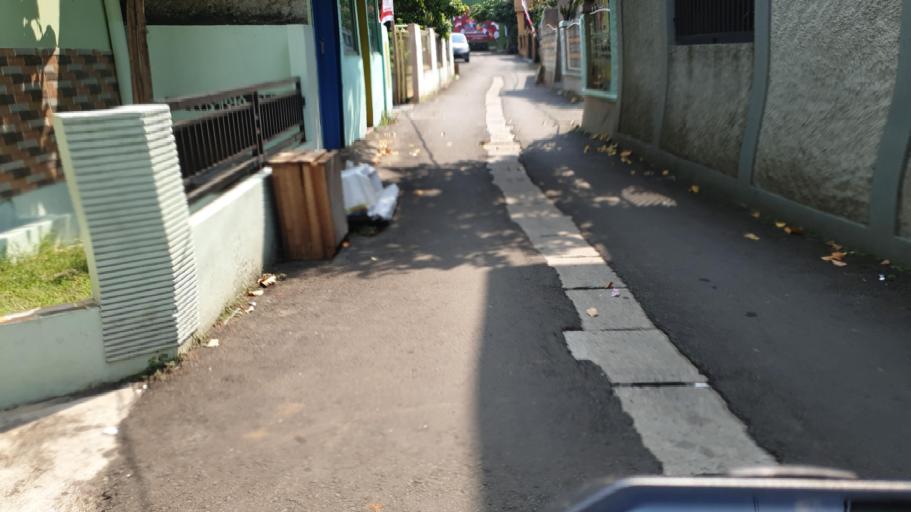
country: ID
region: West Java
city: Depok
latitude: -6.3617
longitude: 106.8356
